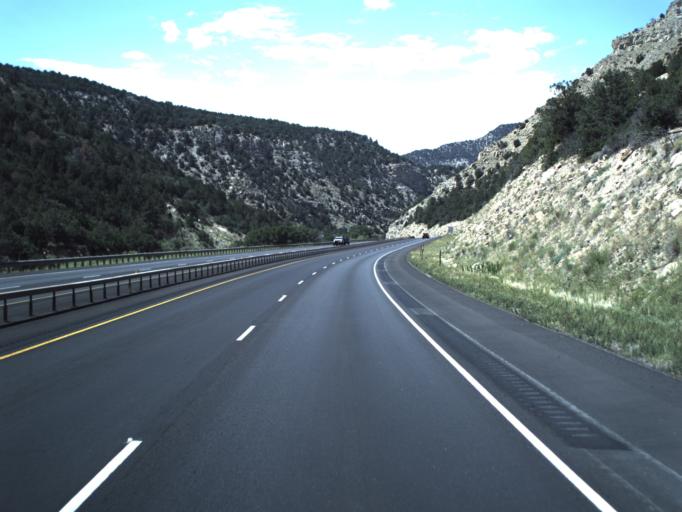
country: US
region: Utah
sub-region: Sevier County
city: Salina
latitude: 38.8928
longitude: -111.6190
